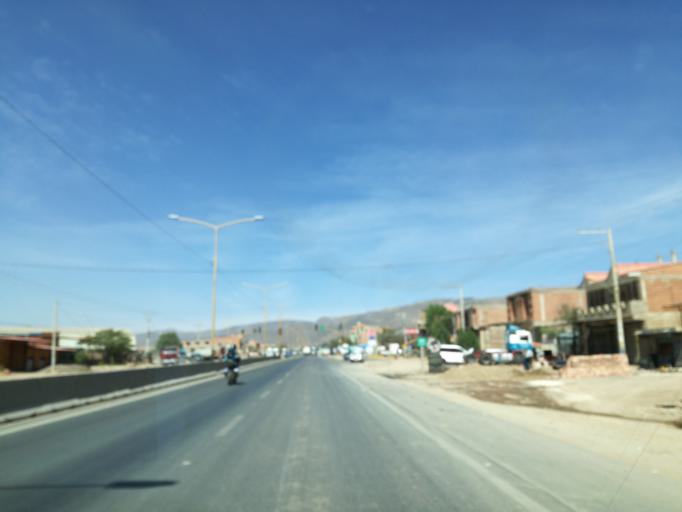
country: BO
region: Cochabamba
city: Sipe Sipe
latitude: -17.4414
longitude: -66.3370
